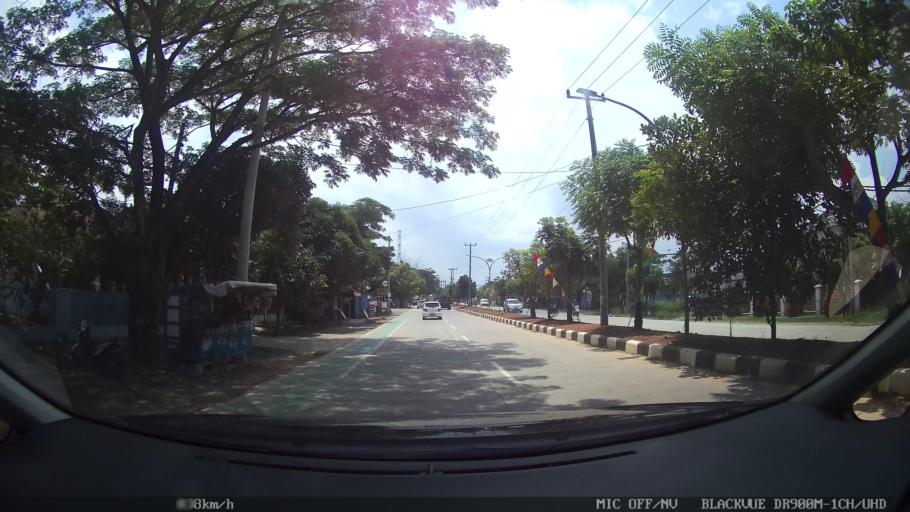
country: ID
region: Lampung
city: Kedaton
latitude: -5.3645
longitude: 105.3019
